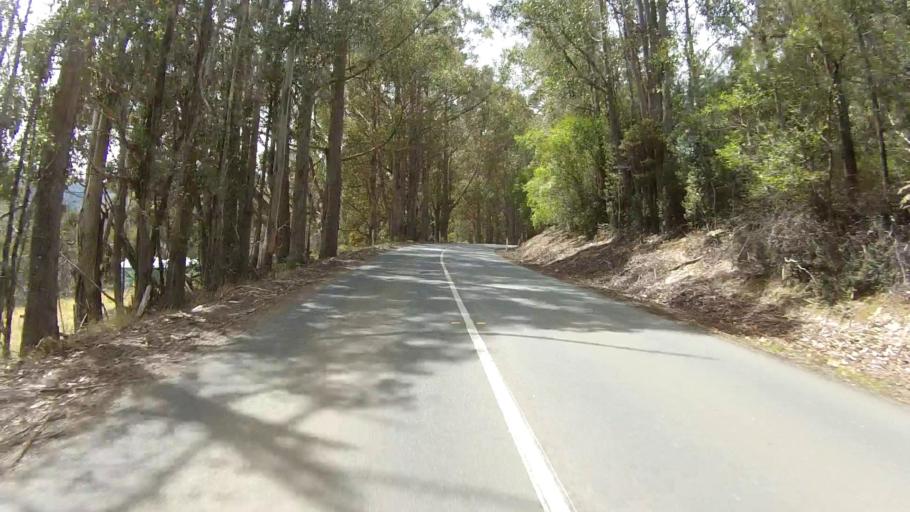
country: AU
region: Tasmania
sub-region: Kingborough
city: Kettering
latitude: -43.1285
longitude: 147.1642
